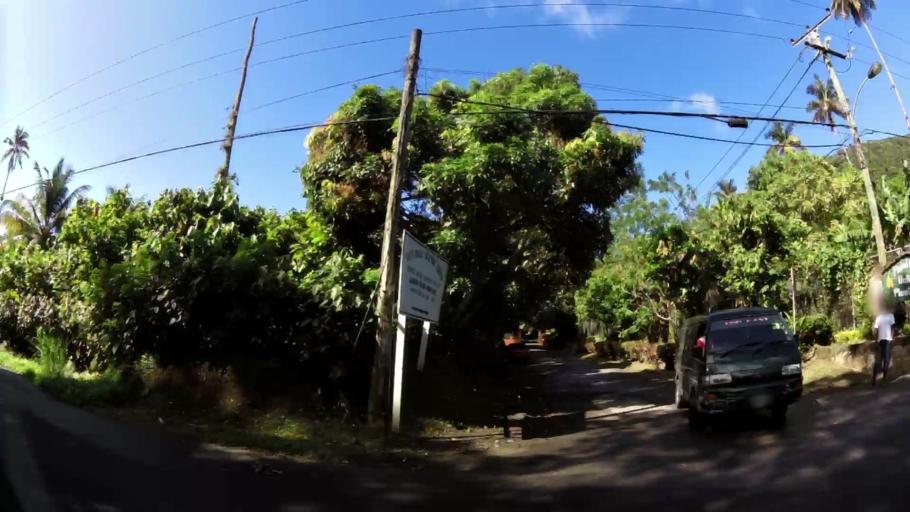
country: LC
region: Soufriere
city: Soufriere
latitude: 13.8222
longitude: -61.0482
